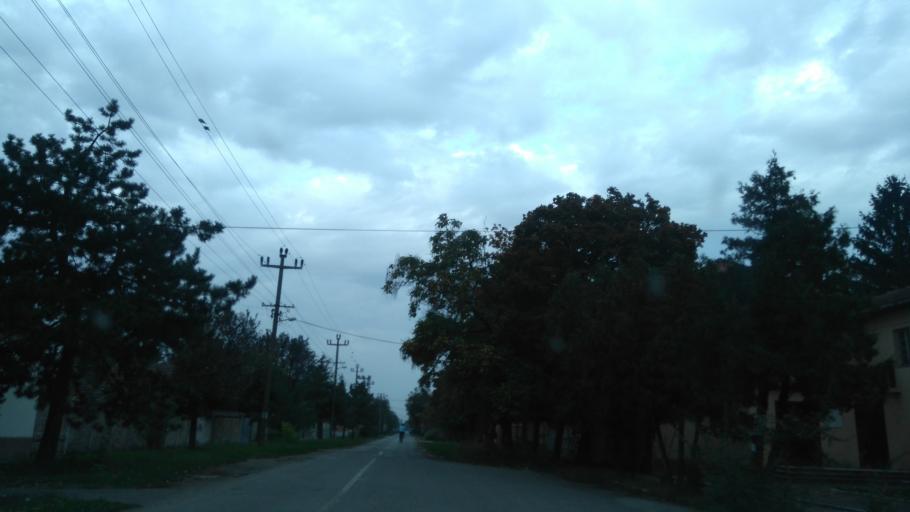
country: RS
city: Mol
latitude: 45.7642
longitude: 20.1362
